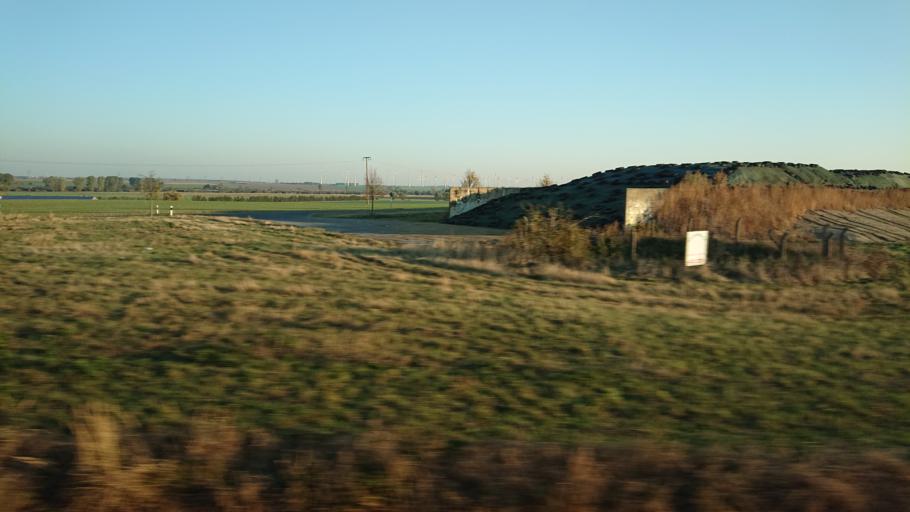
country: DE
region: Mecklenburg-Vorpommern
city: Trollenhagen
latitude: 53.6500
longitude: 13.2881
